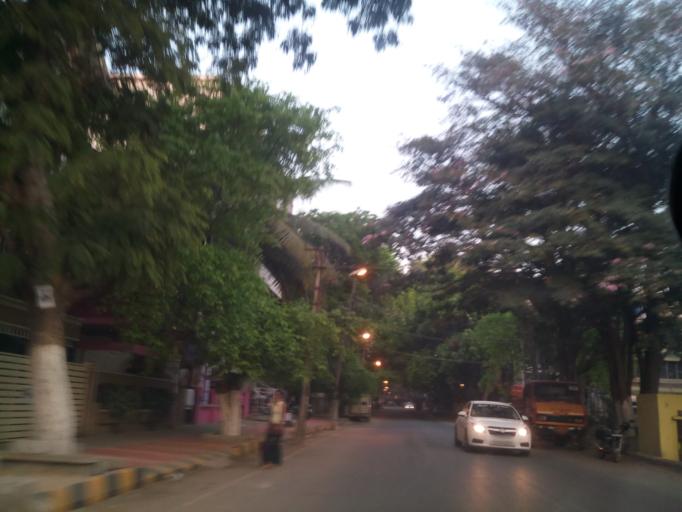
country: IN
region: Karnataka
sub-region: Bangalore Urban
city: Bangalore
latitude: 12.9287
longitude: 77.6358
